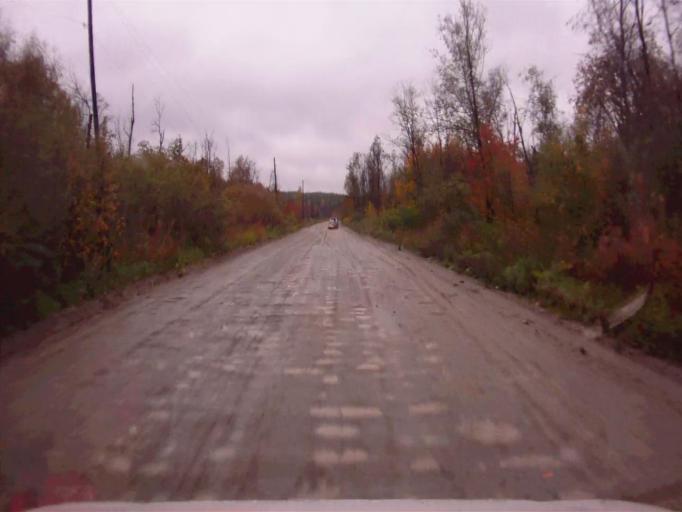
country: RU
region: Chelyabinsk
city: Kyshtym
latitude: 55.7363
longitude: 60.5143
